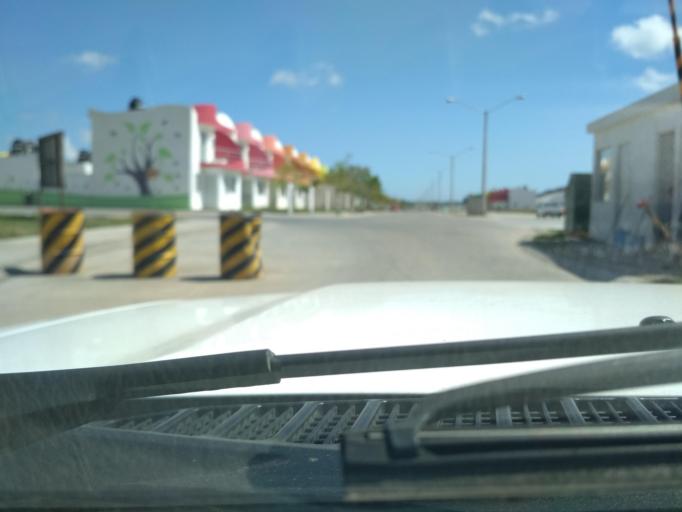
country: MX
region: Veracruz
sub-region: Veracruz
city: Las Amapolas
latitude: 19.1337
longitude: -96.2099
